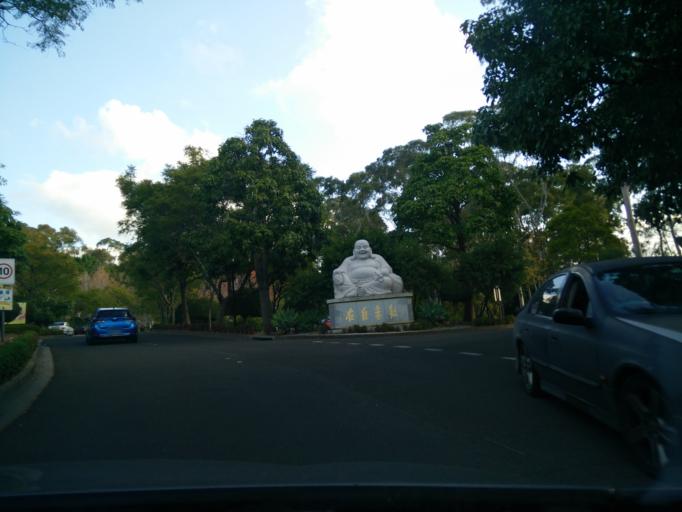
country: AU
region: New South Wales
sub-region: Wollongong
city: Berkeley
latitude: -34.4647
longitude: 150.8504
